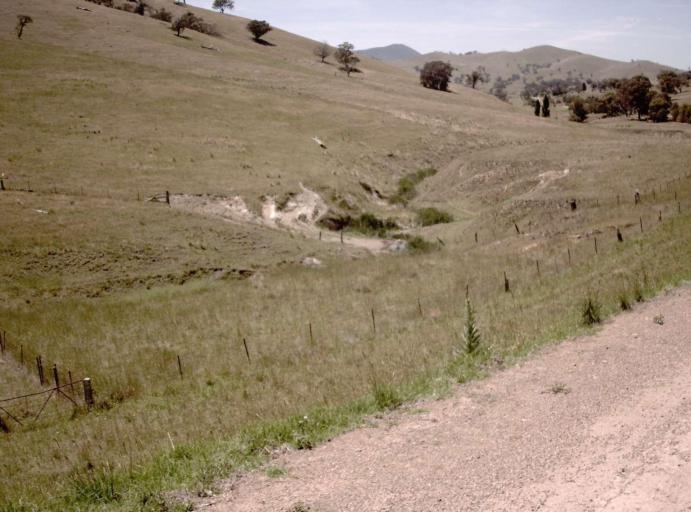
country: AU
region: Victoria
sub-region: East Gippsland
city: Bairnsdale
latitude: -37.3554
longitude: 147.8088
